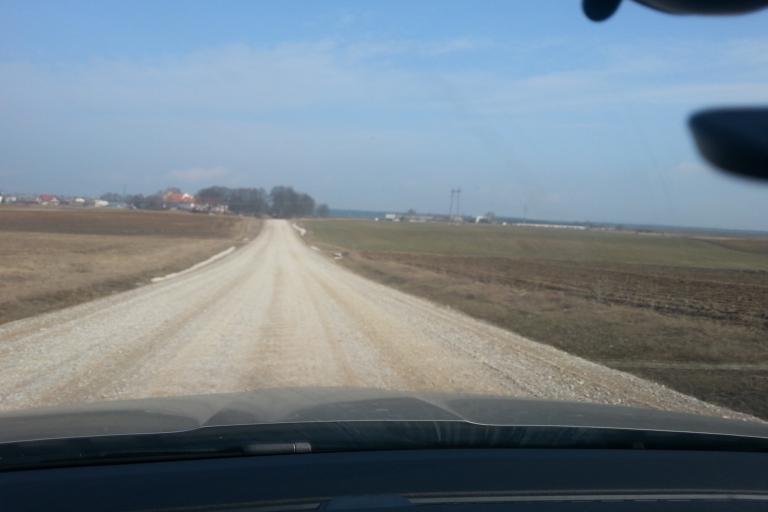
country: LT
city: Trakai
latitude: 54.6001
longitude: 24.9808
